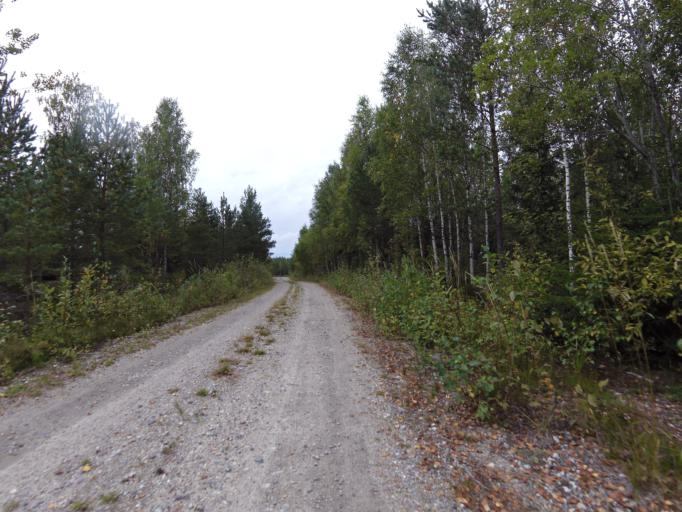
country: SE
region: Gaevleborg
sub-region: Gavle Kommun
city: Valbo
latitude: 60.7447
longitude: 17.0200
